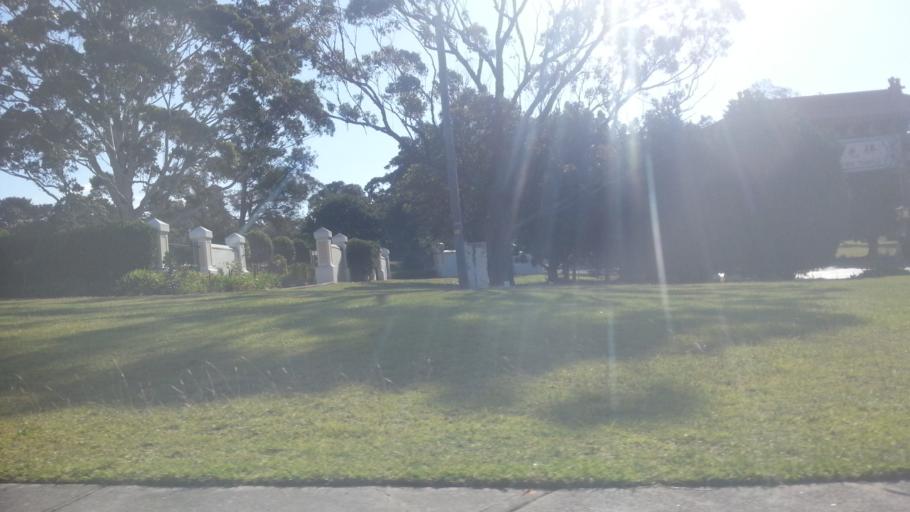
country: AU
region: New South Wales
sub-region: Wollongong
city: Berkeley
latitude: -34.4641
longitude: 150.8543
